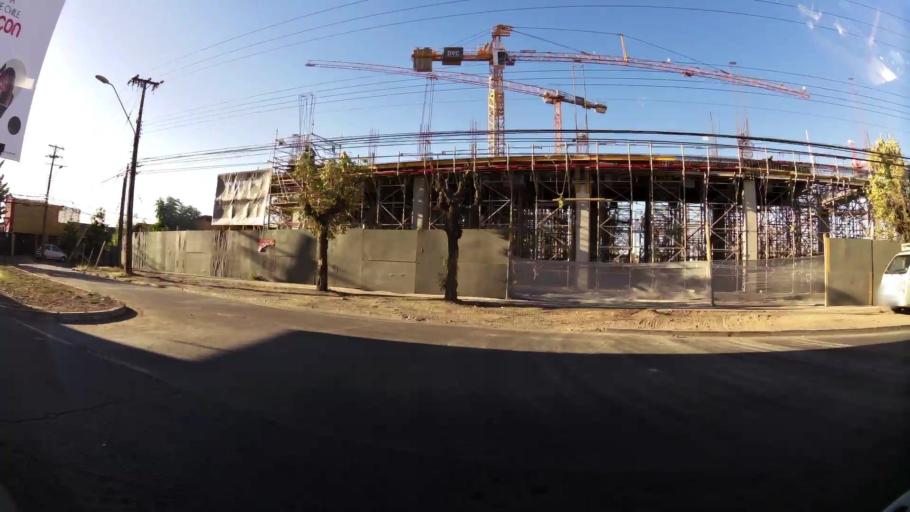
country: CL
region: Maule
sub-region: Provincia de Curico
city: Curico
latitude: -34.9767
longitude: -71.2396
